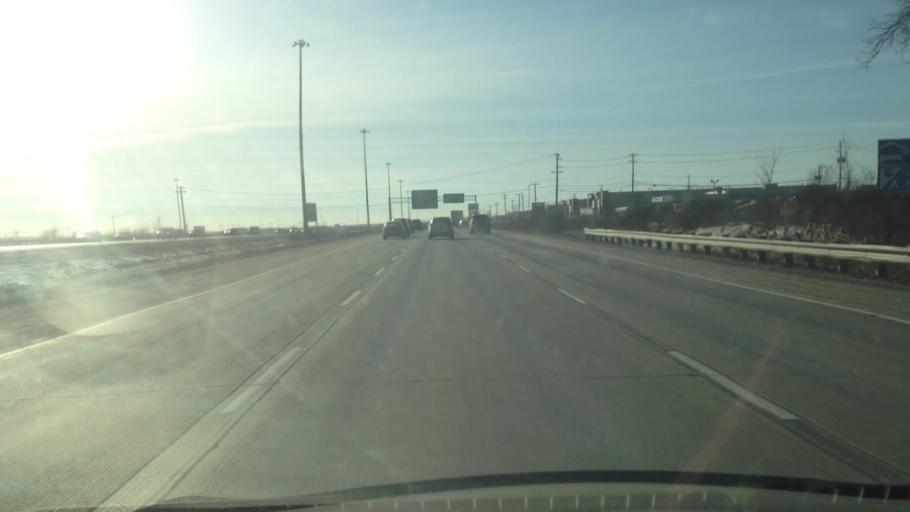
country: CA
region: Quebec
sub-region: Laurentides
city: Saint-Jerome
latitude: 45.7668
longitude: -74.0205
